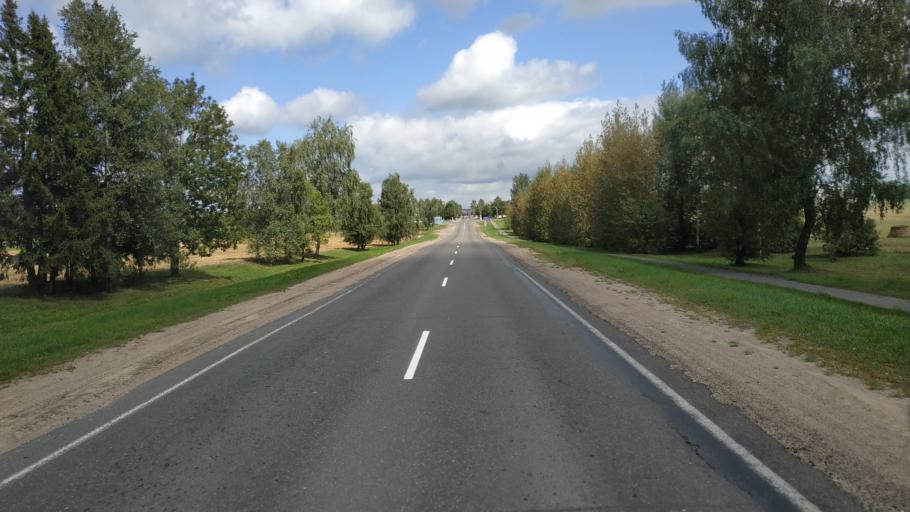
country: BY
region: Mogilev
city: Chavusy
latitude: 53.7993
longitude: 30.9500
